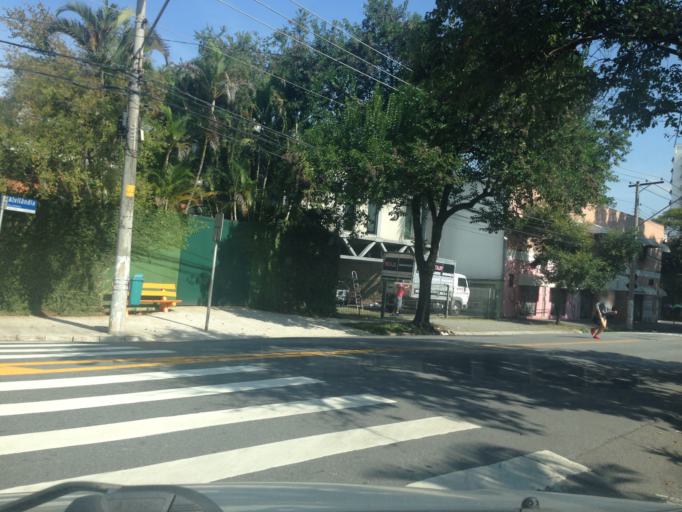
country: BR
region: Sao Paulo
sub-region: Sao Paulo
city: Sao Paulo
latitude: -23.5457
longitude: -46.7076
